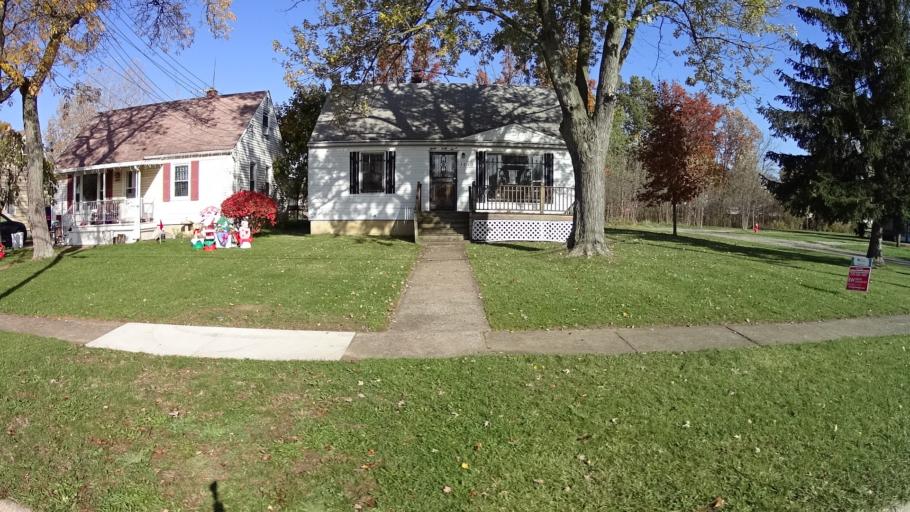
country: US
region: Ohio
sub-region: Lorain County
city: Sheffield Lake
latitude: 41.4683
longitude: -82.1377
